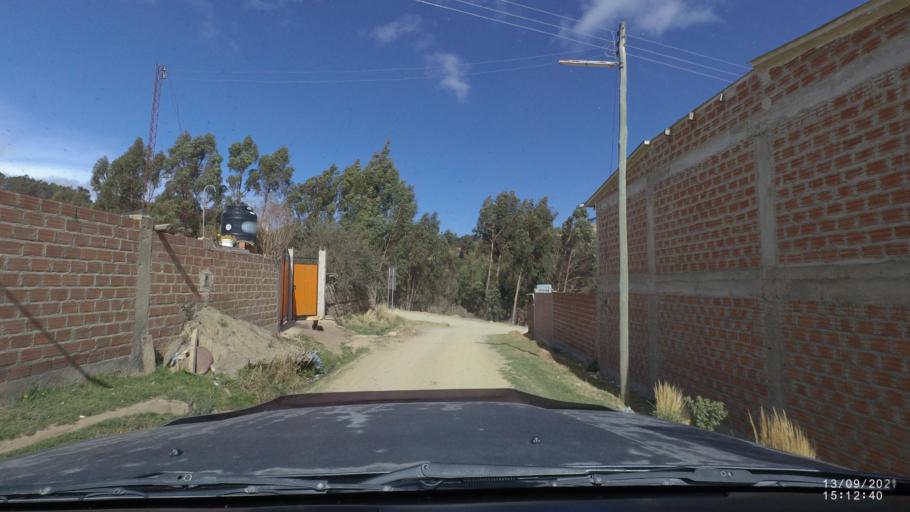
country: BO
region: Cochabamba
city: Colomi
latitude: -17.3627
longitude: -65.8059
